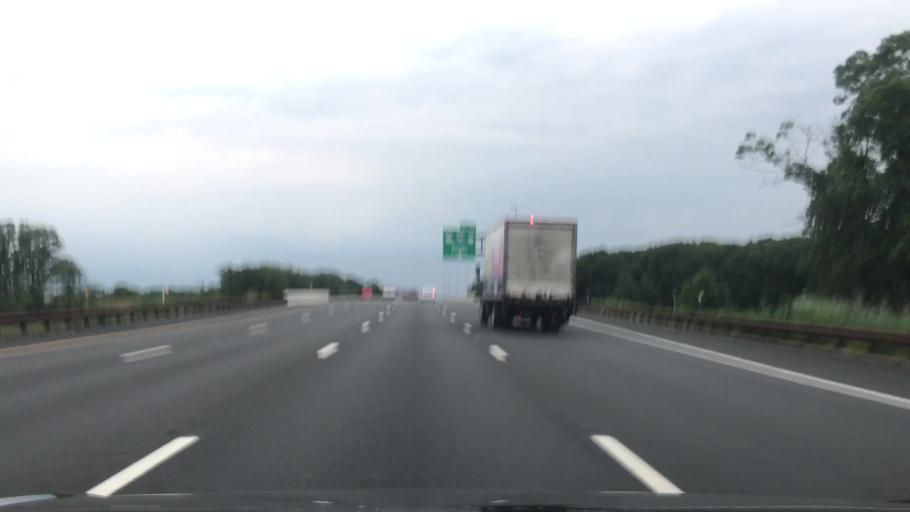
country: US
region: New Jersey
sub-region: Monmouth County
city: Ramtown
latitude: 40.1594
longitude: -74.1024
